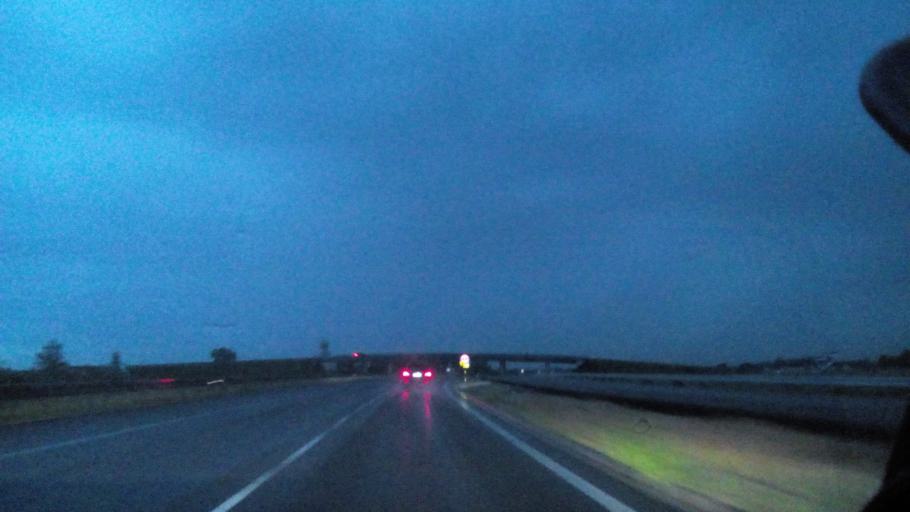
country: PL
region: Kujawsko-Pomorskie
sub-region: Powiat nakielski
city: Szubin
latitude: 53.0094
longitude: 17.7668
